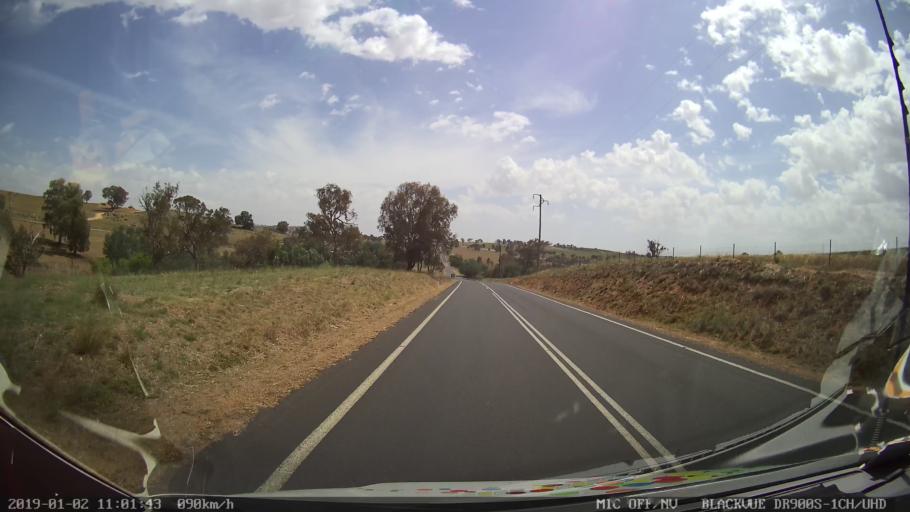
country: AU
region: New South Wales
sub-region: Young
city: Young
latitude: -34.5947
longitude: 148.3218
